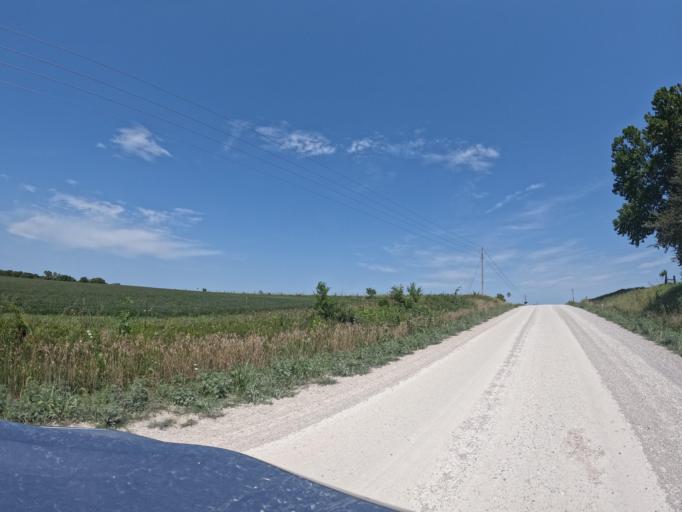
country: US
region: Iowa
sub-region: Henry County
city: Mount Pleasant
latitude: 40.9085
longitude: -91.6658
